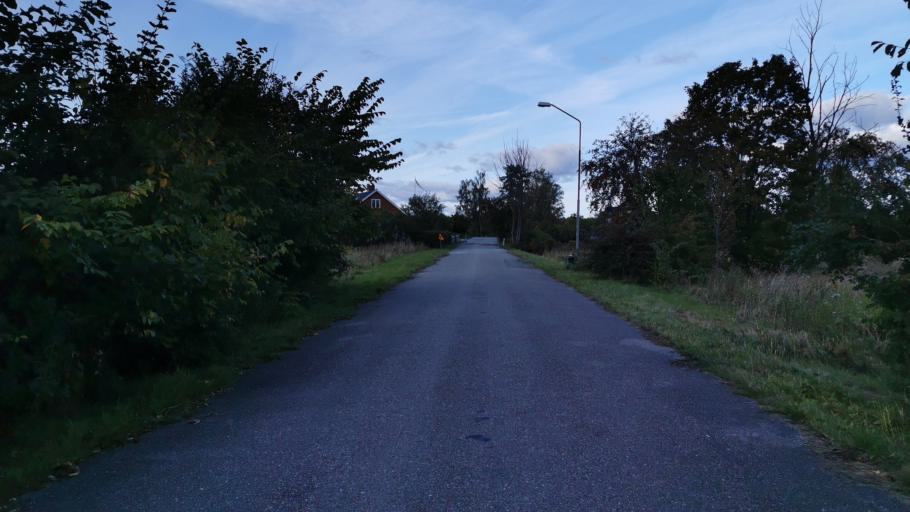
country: SE
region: OErebro
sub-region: Orebro Kommun
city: Hovsta
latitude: 59.3127
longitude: 15.2263
